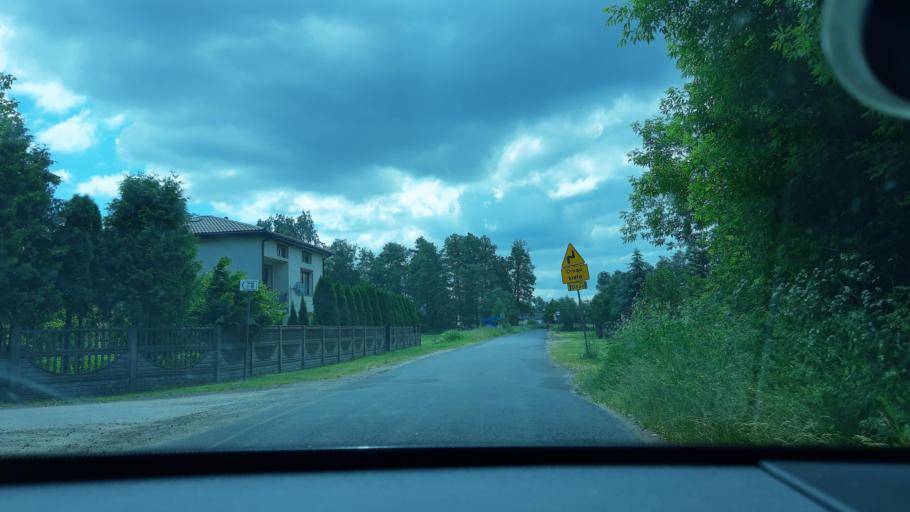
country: PL
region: Lodz Voivodeship
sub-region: Powiat zdunskowolski
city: Zapolice
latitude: 51.5295
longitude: 18.8379
